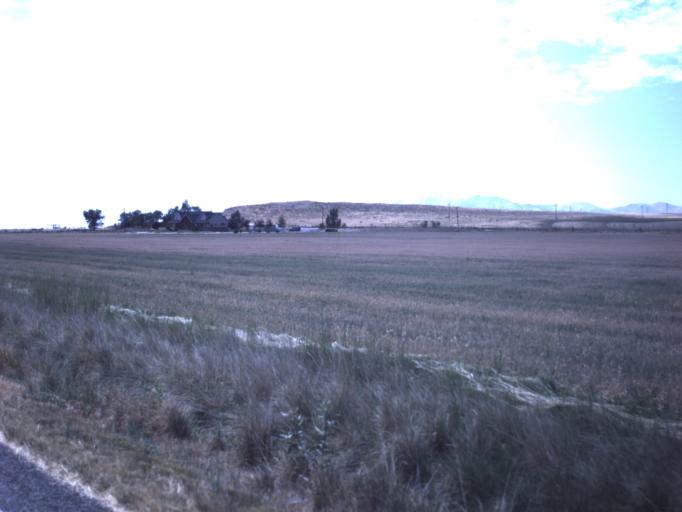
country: US
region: Utah
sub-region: Box Elder County
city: Tremonton
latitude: 41.6315
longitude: -112.3309
